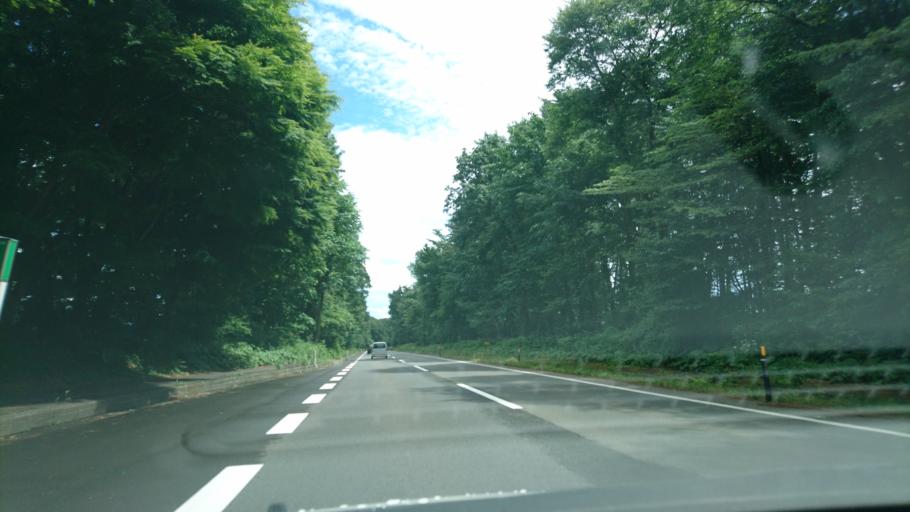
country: JP
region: Iwate
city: Morioka-shi
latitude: 39.7881
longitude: 141.1235
